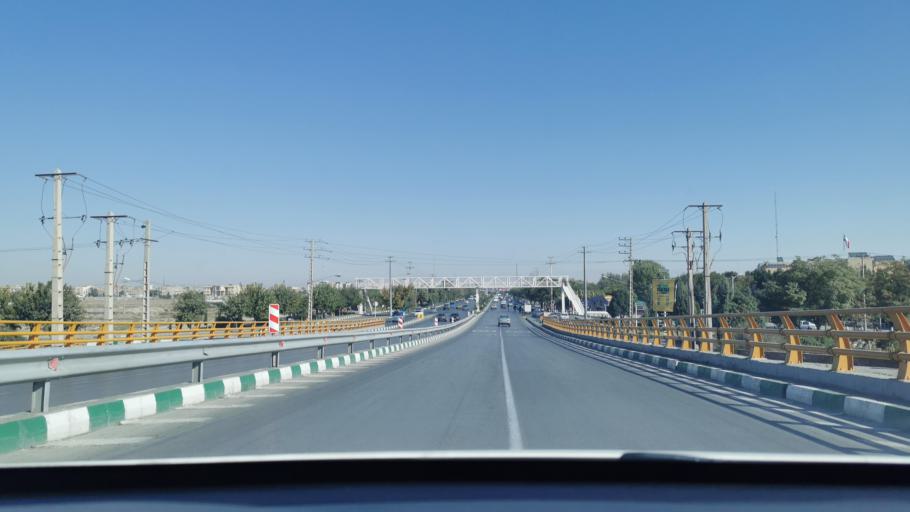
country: IR
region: Razavi Khorasan
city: Mashhad
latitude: 36.3300
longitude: 59.6246
